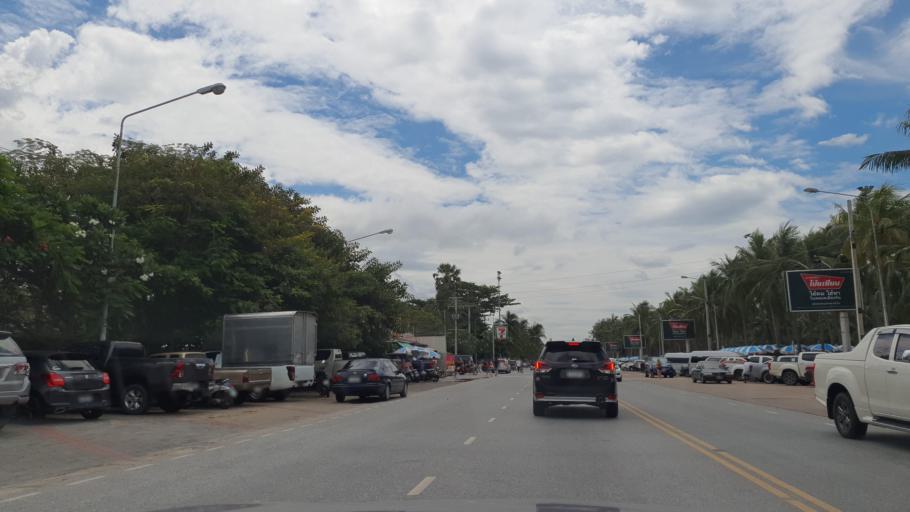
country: TH
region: Chon Buri
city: Chon Buri
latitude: 13.2966
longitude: 100.9045
